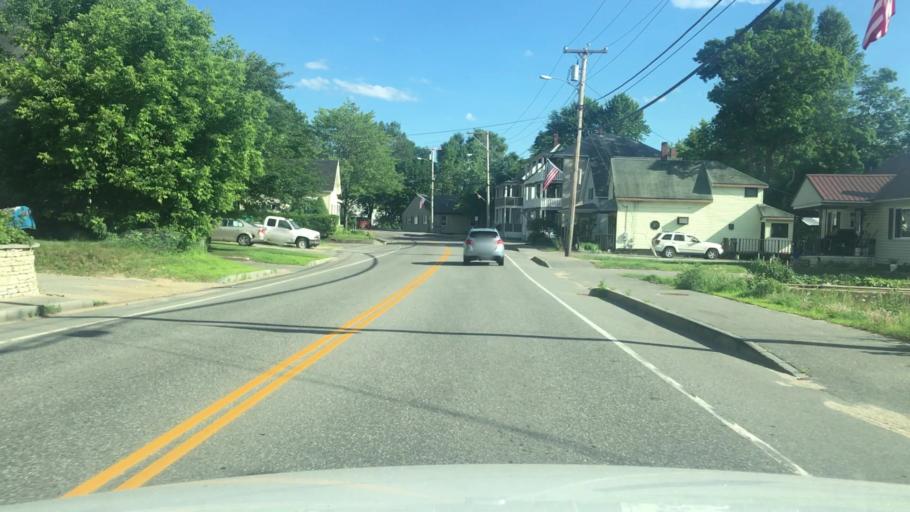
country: US
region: Maine
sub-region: Franklin County
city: Chisholm
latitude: 44.4827
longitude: -70.2003
